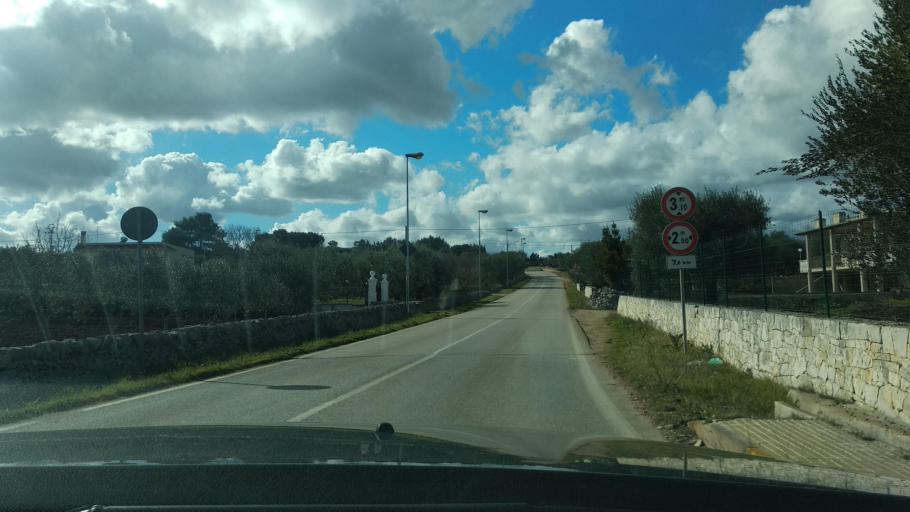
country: IT
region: Apulia
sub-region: Provincia di Brindisi
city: Casalini
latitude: 40.7007
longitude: 17.4911
